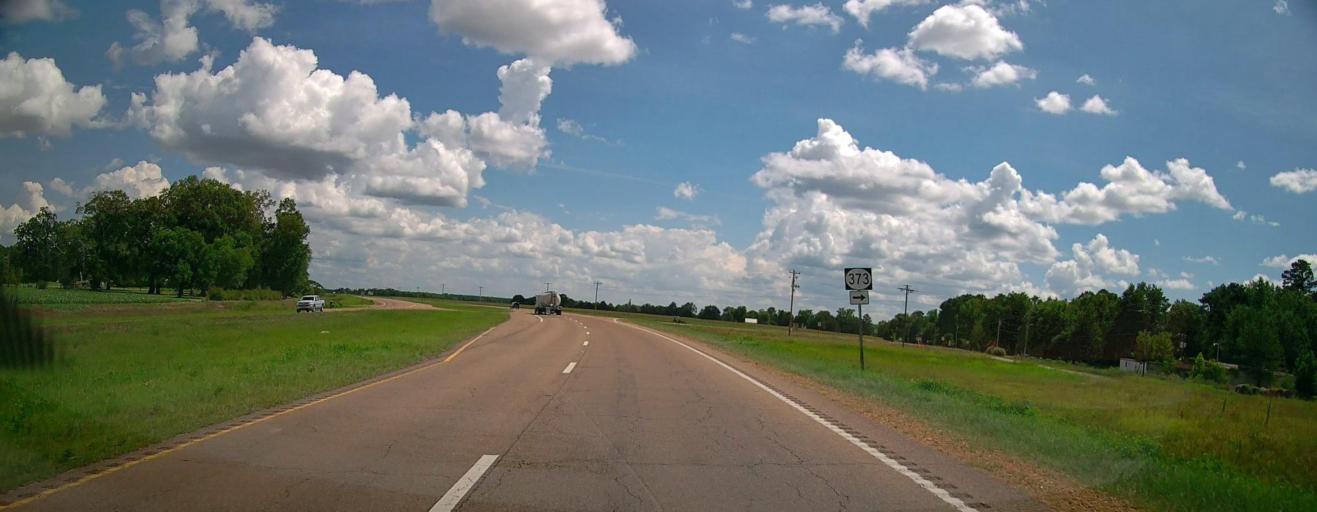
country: US
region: Mississippi
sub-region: Lowndes County
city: Columbus Air Force Base
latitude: 33.7142
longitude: -88.4513
